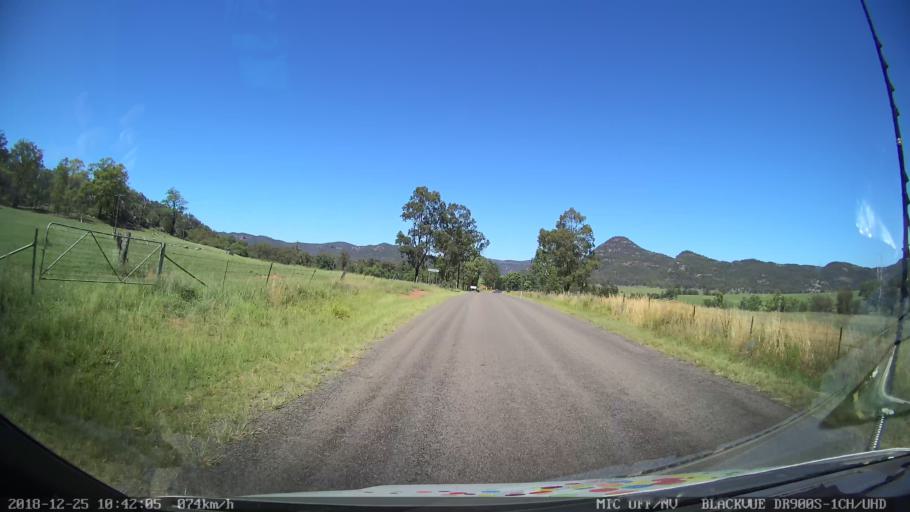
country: AU
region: New South Wales
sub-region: Upper Hunter Shire
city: Merriwa
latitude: -32.4145
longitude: 150.3278
